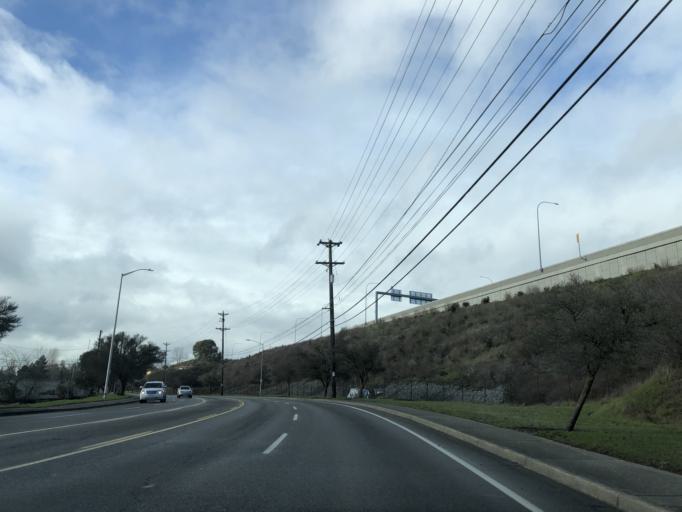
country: US
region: Washington
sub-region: Pierce County
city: Tacoma
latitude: 47.2341
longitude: -122.4689
